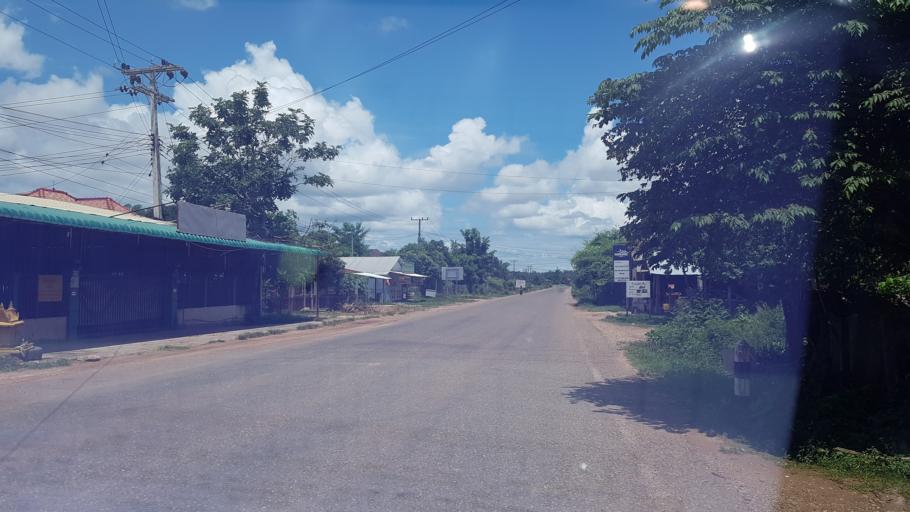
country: LA
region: Vientiane
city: Vientiane
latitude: 18.1069
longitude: 102.5756
